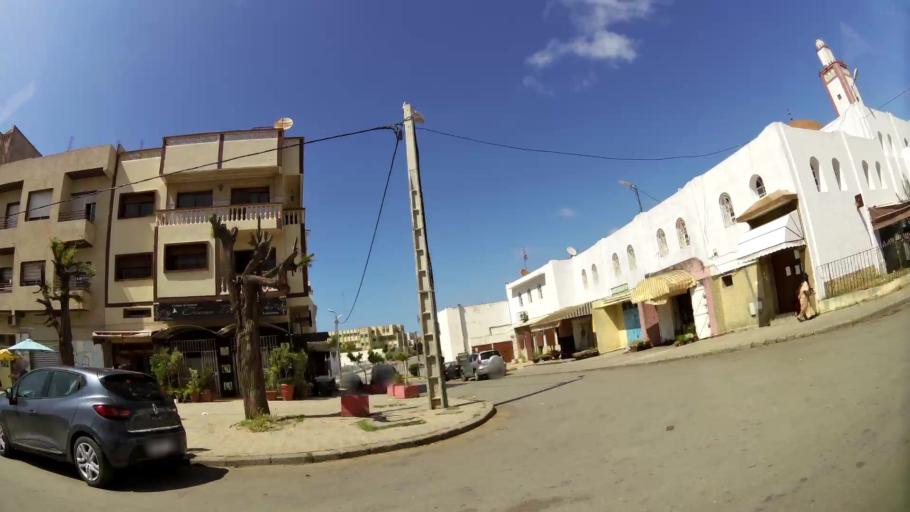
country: MA
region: Rabat-Sale-Zemmour-Zaer
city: Sale
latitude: 34.0427
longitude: -6.7880
